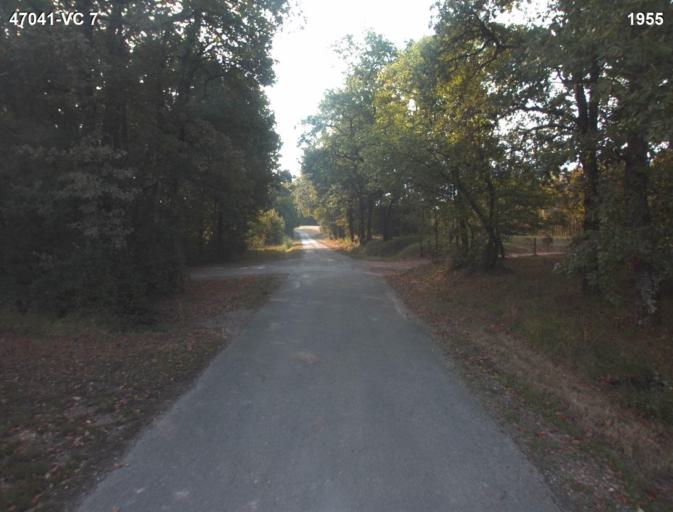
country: FR
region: Aquitaine
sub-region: Departement du Lot-et-Garonne
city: Port-Sainte-Marie
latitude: 44.1935
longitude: 0.4202
